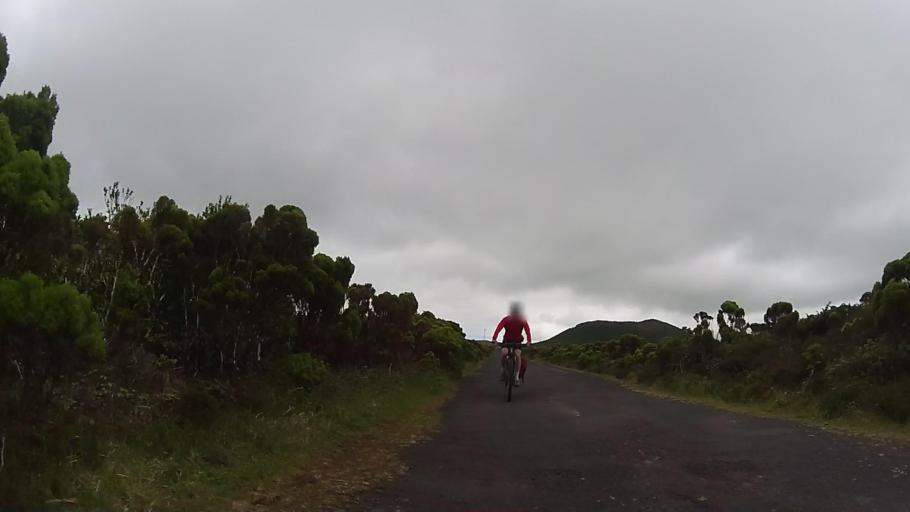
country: PT
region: Azores
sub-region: Sao Roque do Pico
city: Sao Roque do Pico
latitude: 38.4643
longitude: -28.2853
